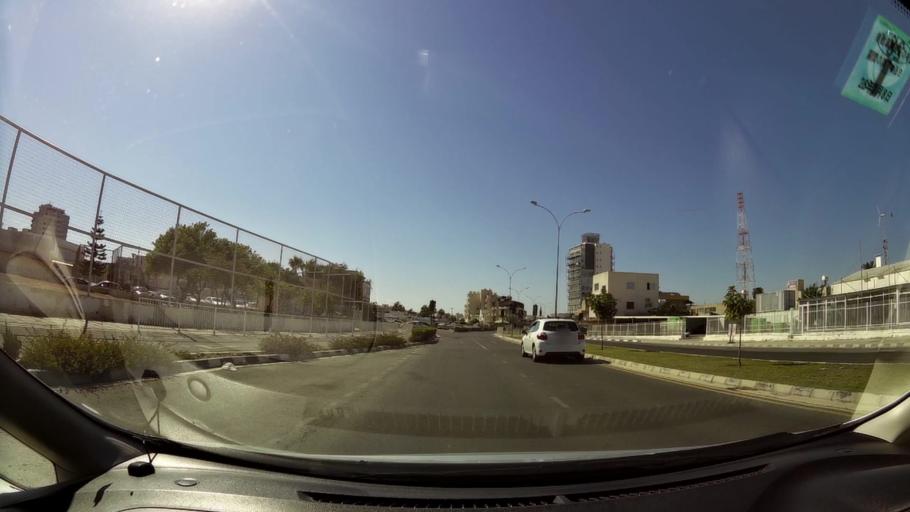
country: CY
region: Larnaka
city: Larnaca
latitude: 34.9329
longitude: 33.6282
